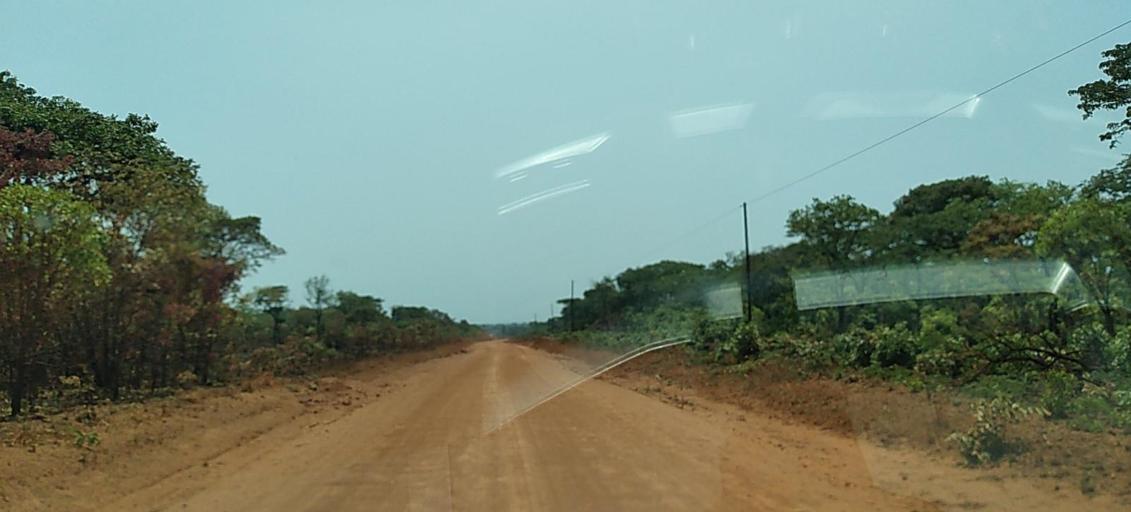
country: CD
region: Katanga
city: Kipushi
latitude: -11.9399
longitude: 26.9477
